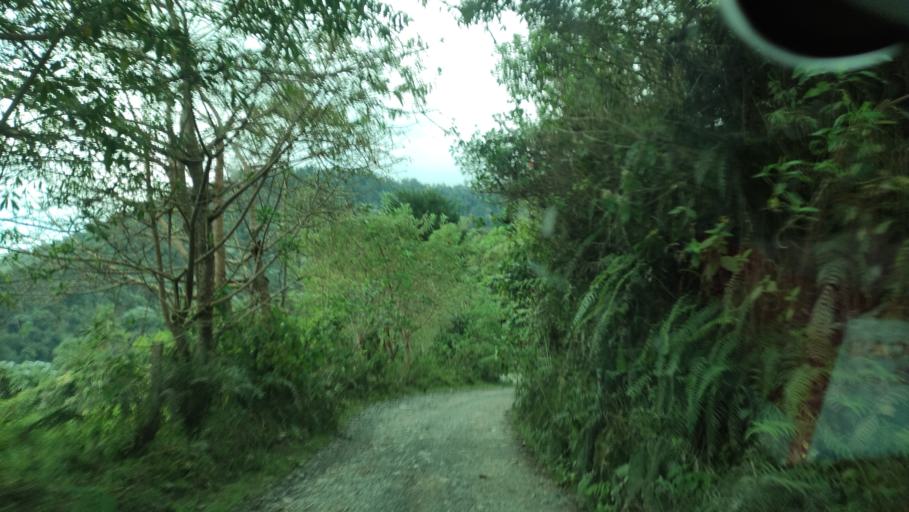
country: CO
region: Valle del Cauca
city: San Pedro
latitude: 3.8777
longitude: -76.1498
